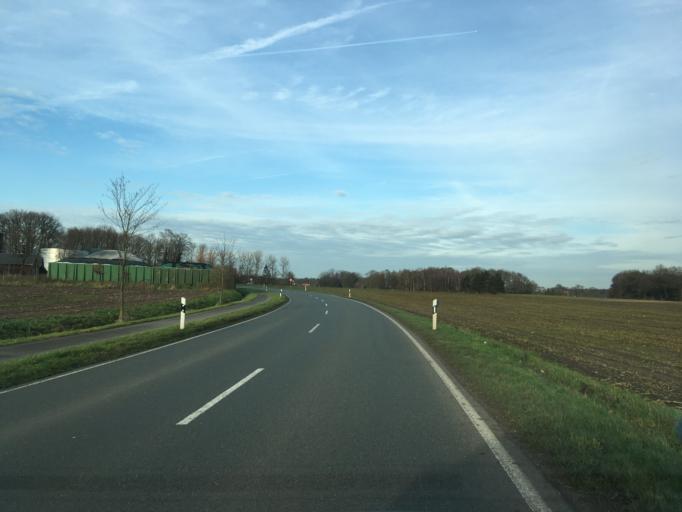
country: DE
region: North Rhine-Westphalia
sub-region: Regierungsbezirk Munster
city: Gescher
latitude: 52.0048
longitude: 7.0369
